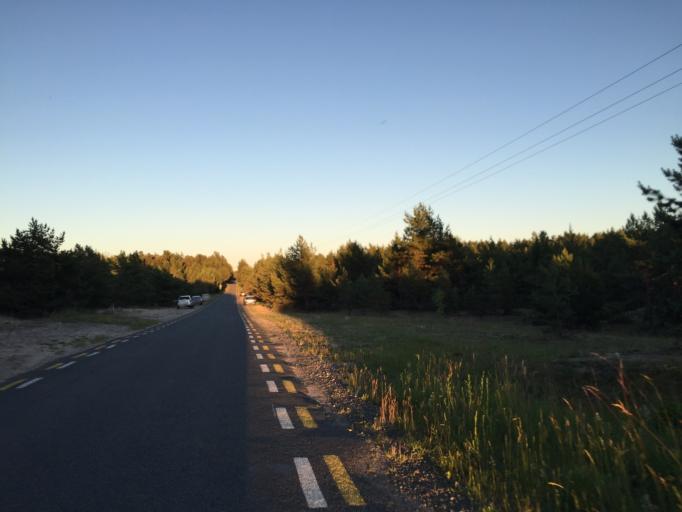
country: EE
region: Harju
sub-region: Raasiku vald
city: Raasiku
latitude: 59.5079
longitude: 25.2776
